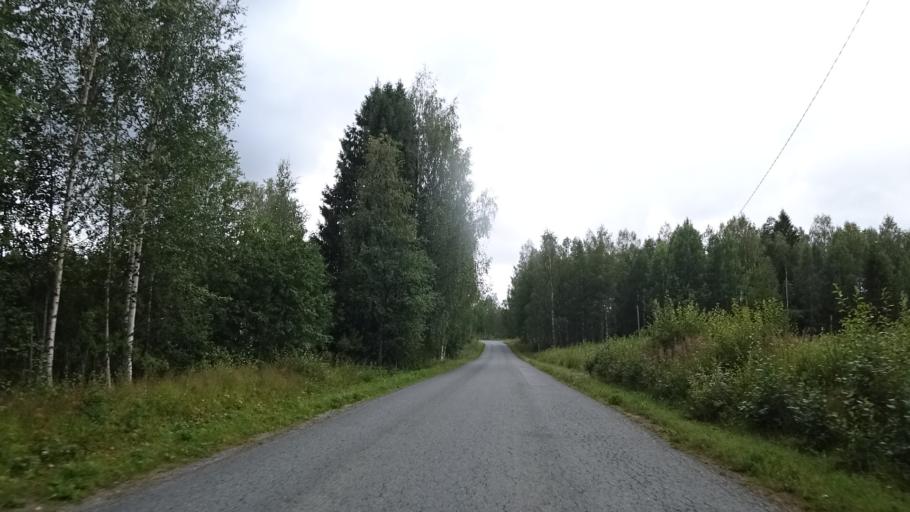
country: FI
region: North Karelia
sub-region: Joensuu
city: Ilomantsi
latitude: 62.9427
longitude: 31.2926
